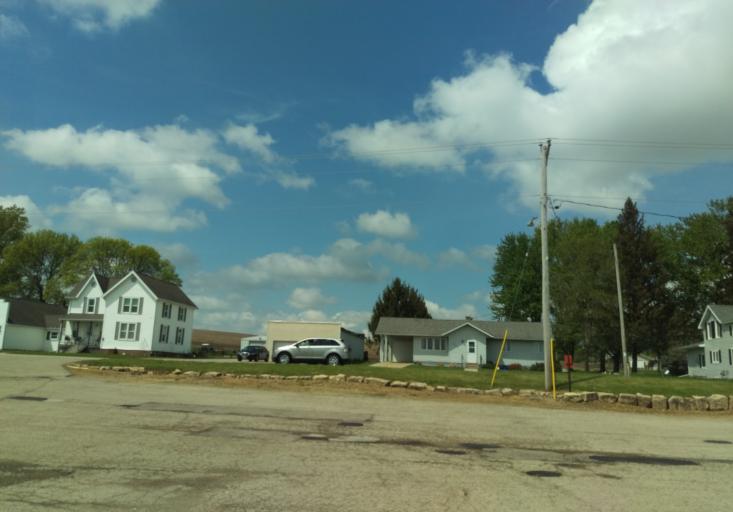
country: US
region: Wisconsin
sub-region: Dane County
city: Cross Plains
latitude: 43.0596
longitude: -89.6554
